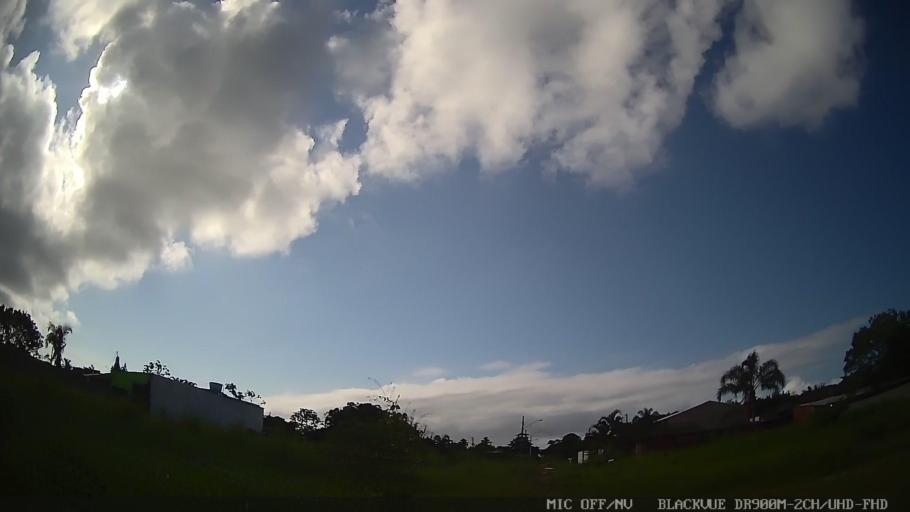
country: BR
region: Sao Paulo
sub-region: Peruibe
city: Peruibe
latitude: -24.2695
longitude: -46.9432
